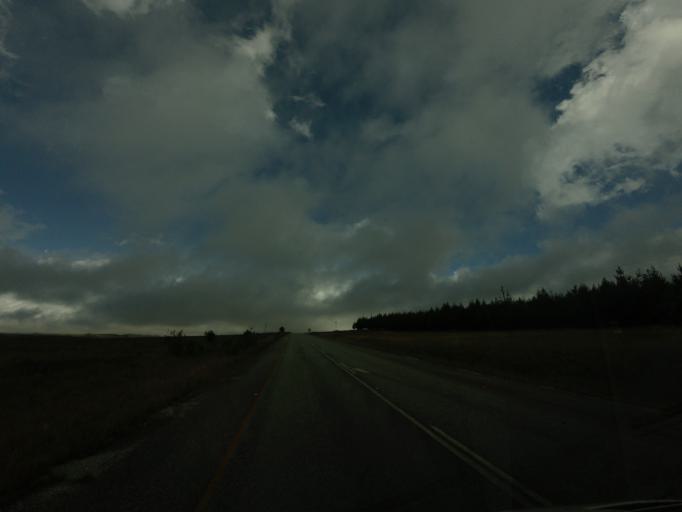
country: ZA
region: Mpumalanga
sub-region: Ehlanzeni District
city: Graksop
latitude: -24.8562
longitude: 30.8745
